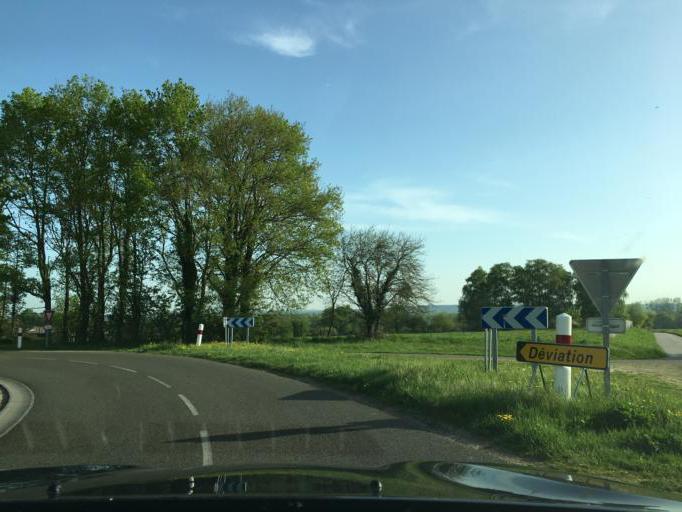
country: FR
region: Ile-de-France
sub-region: Departement des Yvelines
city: Conde-sur-Vesgre
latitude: 48.7151
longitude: 1.6628
